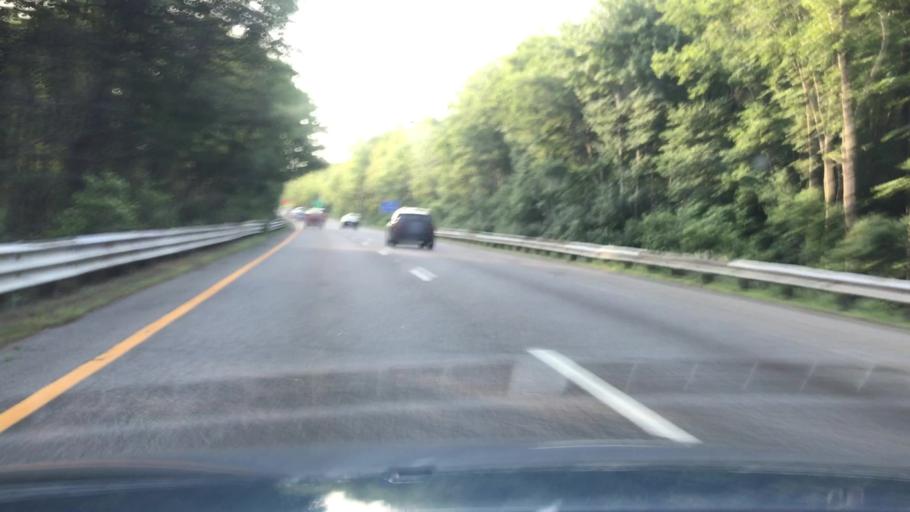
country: US
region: Massachusetts
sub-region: Plymouth County
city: Rockland
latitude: 42.1701
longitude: -70.9044
